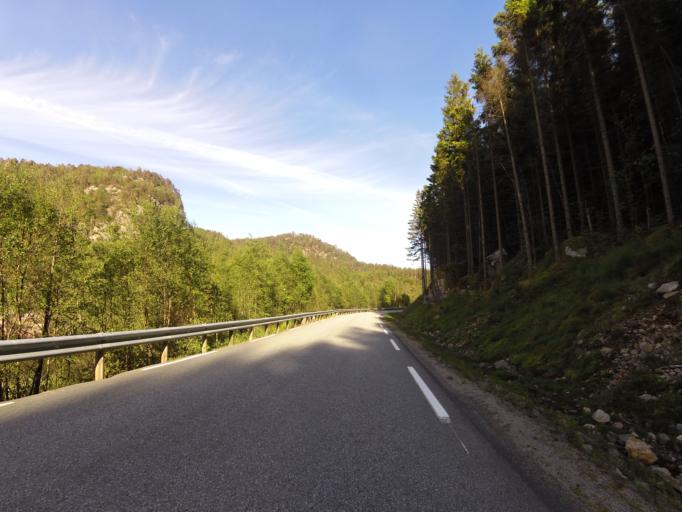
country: NO
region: Vest-Agder
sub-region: Flekkefjord
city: Flekkefjord
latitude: 58.2821
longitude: 6.6206
